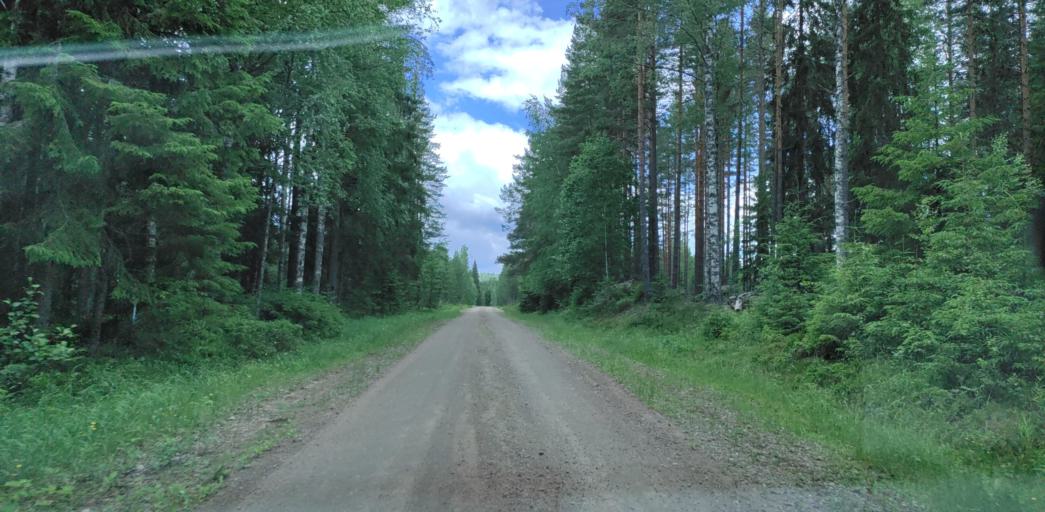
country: SE
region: Vaermland
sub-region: Hagfors Kommun
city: Ekshaerad
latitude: 60.0896
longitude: 13.4184
